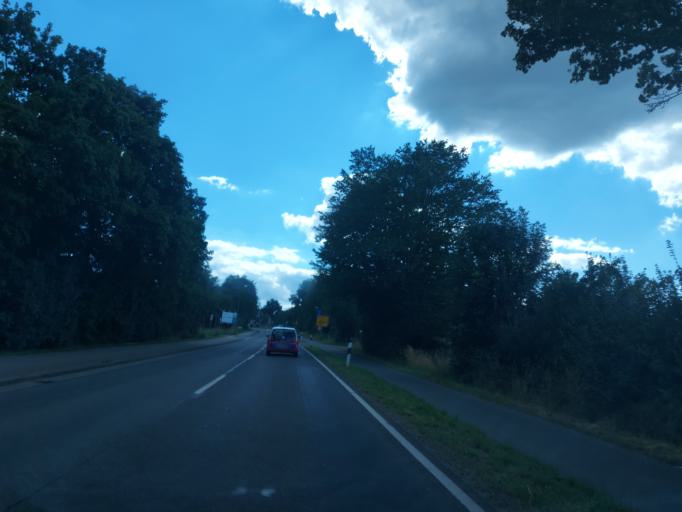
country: DE
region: Lower Saxony
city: Georgsmarienhutte
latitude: 52.2299
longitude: 8.0161
